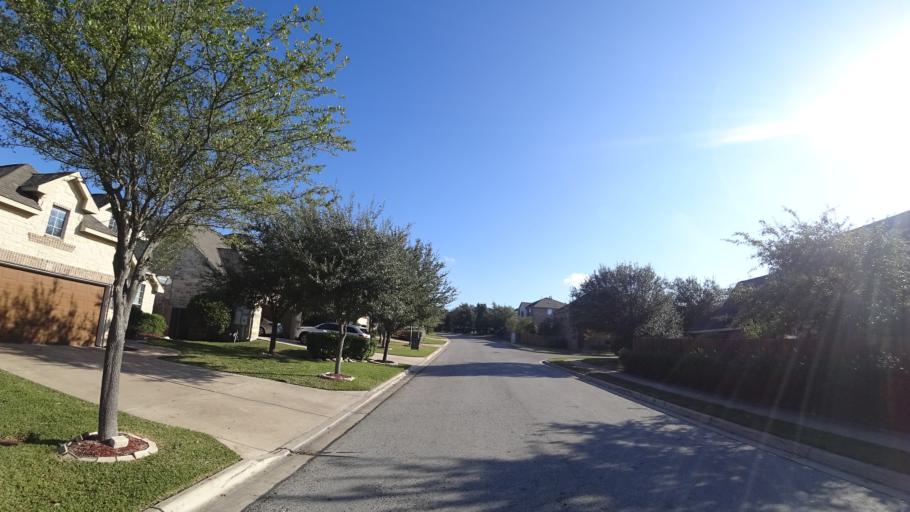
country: US
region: Texas
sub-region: Travis County
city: Hudson Bend
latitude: 30.3683
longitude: -97.8966
